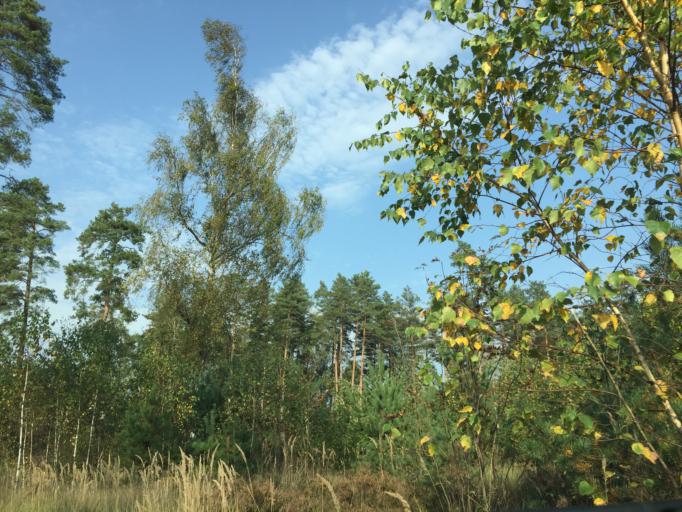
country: LV
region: Garkalne
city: Garkalne
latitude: 56.9583
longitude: 24.4262
